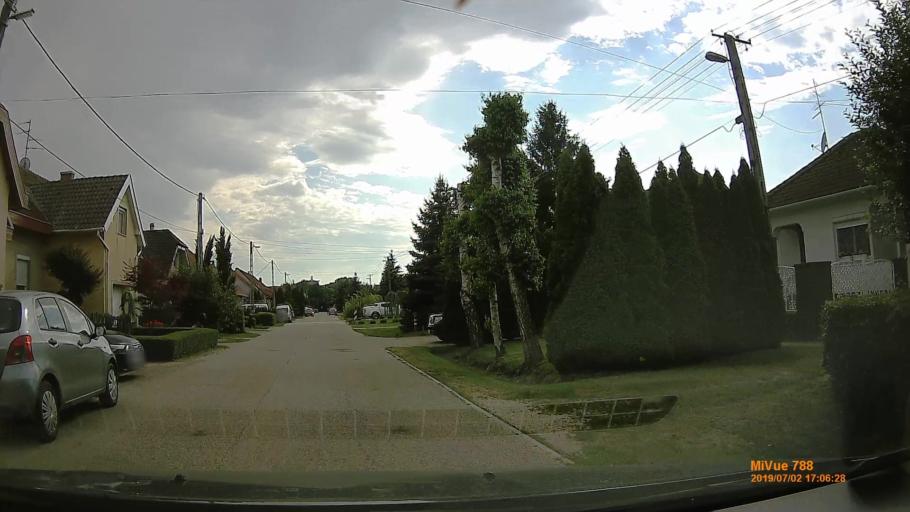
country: HU
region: Gyor-Moson-Sopron
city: Mosonmagyarovar
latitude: 47.8764
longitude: 17.2882
